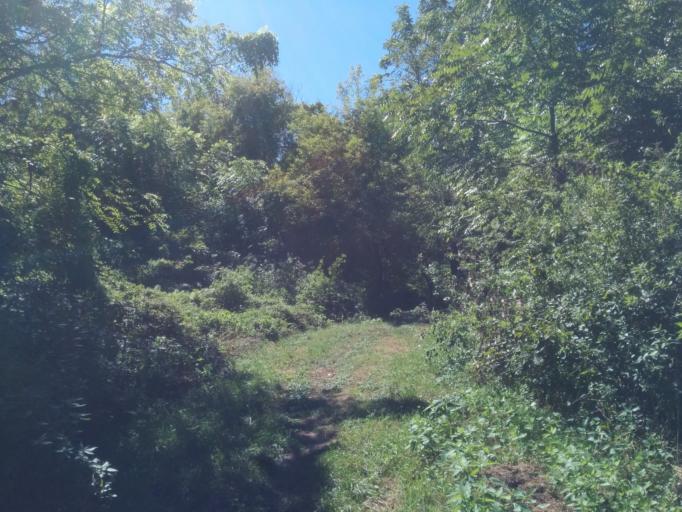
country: US
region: Illinois
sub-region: Cook County
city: Western Springs
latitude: 41.8205
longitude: -87.9063
